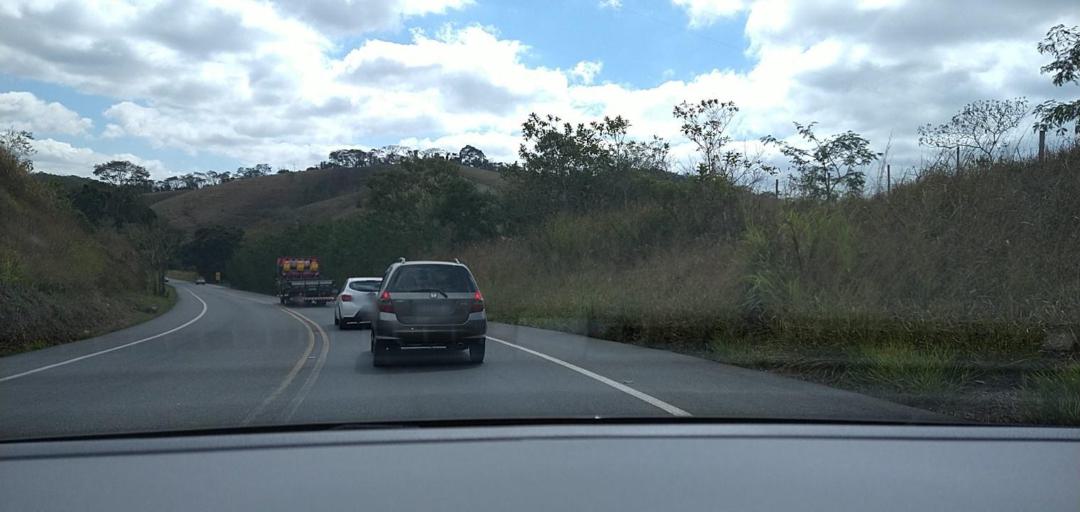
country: BR
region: Minas Gerais
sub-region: Ponte Nova
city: Ponte Nova
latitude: -20.5025
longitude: -42.8769
